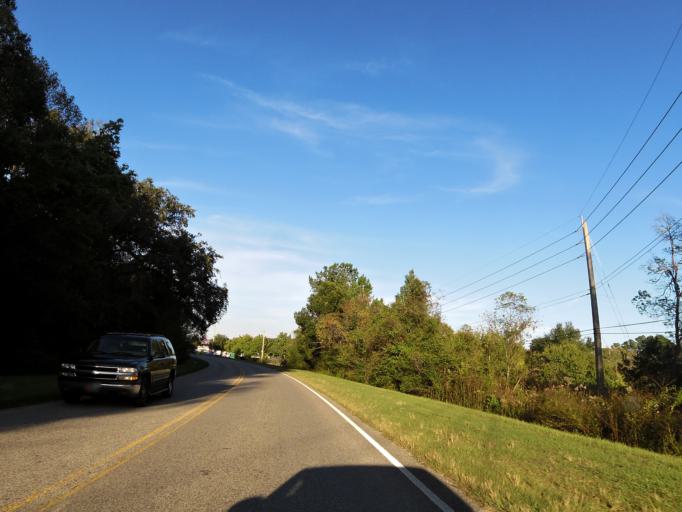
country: US
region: Florida
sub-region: Duval County
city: Jacksonville
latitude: 30.3298
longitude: -81.7662
